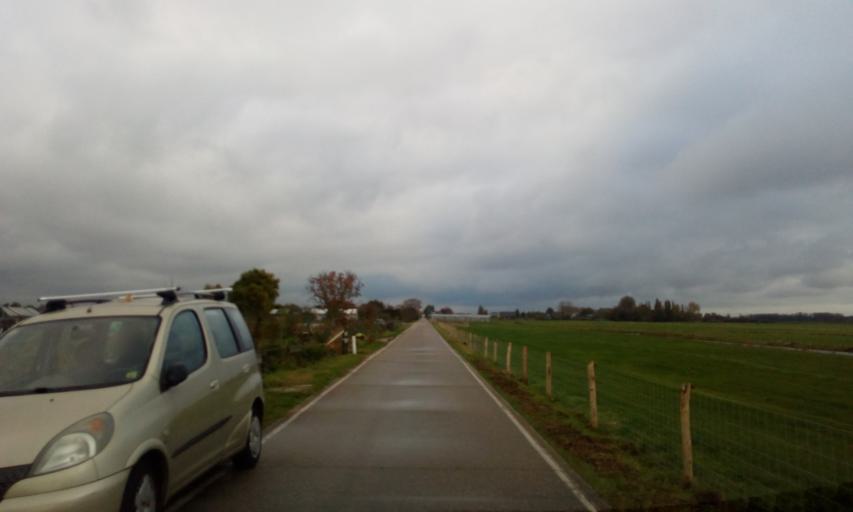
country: NL
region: South Holland
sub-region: Gemeente Pijnacker-Nootdorp
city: Pijnacker
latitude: 51.9678
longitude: 4.4237
